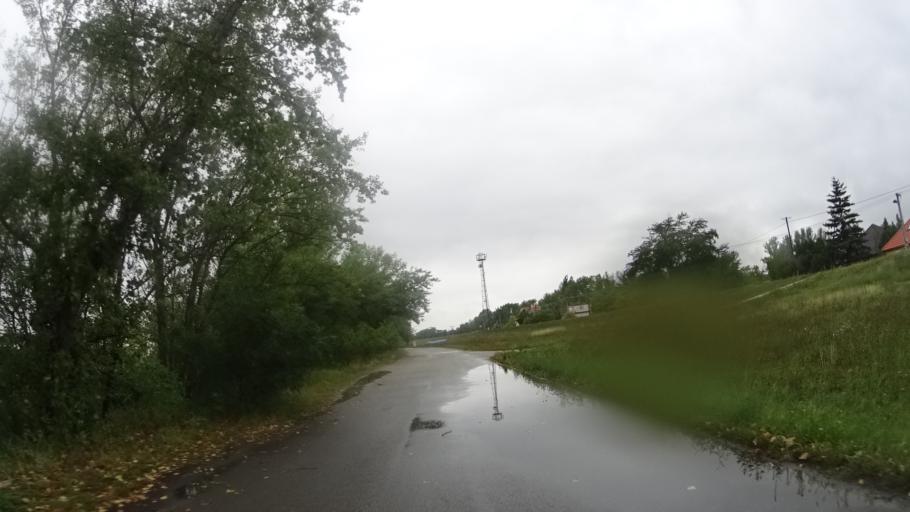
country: HU
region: Komarom-Esztergom
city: Sutto
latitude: 47.7648
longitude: 18.4723
